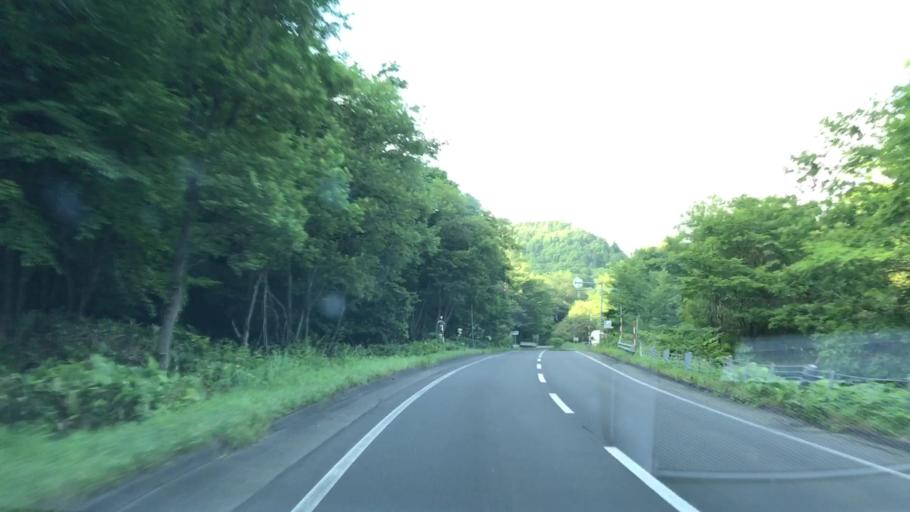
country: JP
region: Hokkaido
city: Chitose
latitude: 42.8904
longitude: 142.1228
